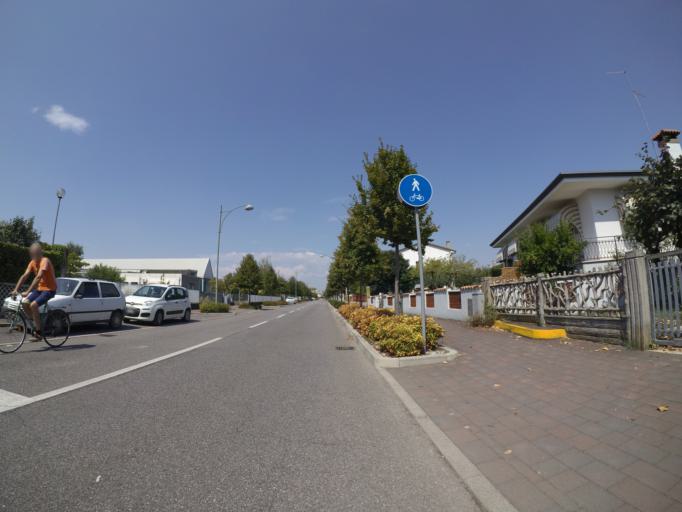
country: IT
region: Friuli Venezia Giulia
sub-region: Provincia di Udine
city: Codroipo
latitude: 45.9567
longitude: 12.9850
